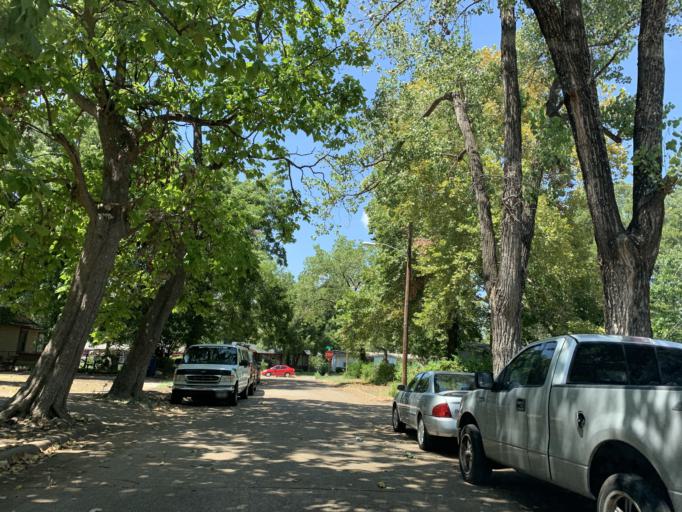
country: US
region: Texas
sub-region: Dallas County
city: Hutchins
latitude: 32.7008
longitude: -96.7650
